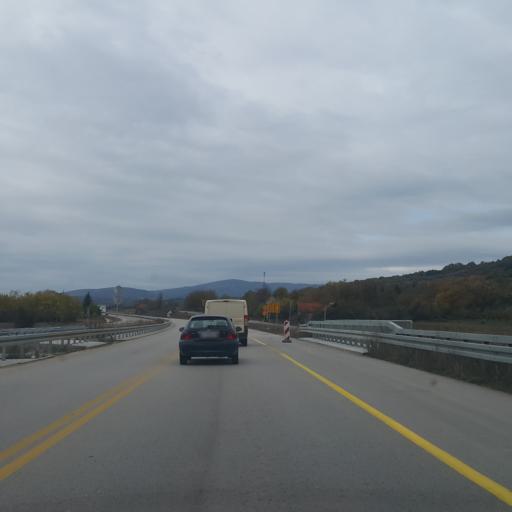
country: RS
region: Central Serbia
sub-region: Pirotski Okrug
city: Pirot
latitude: 43.2202
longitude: 22.4959
